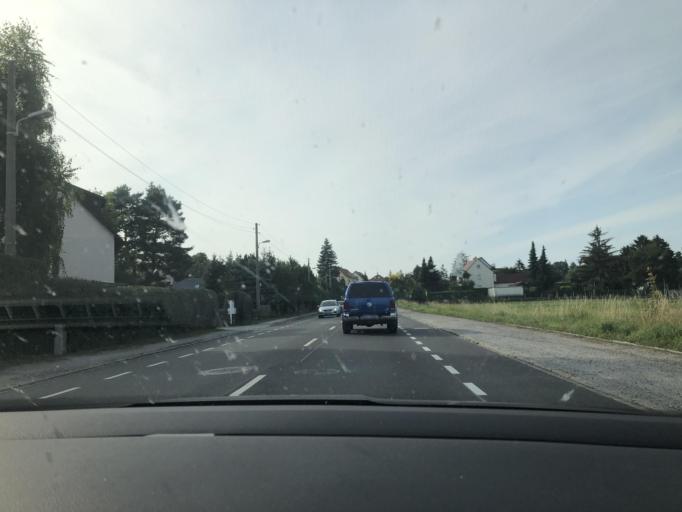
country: DE
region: Saxony
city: Albertstadt
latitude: 51.1114
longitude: 13.7303
